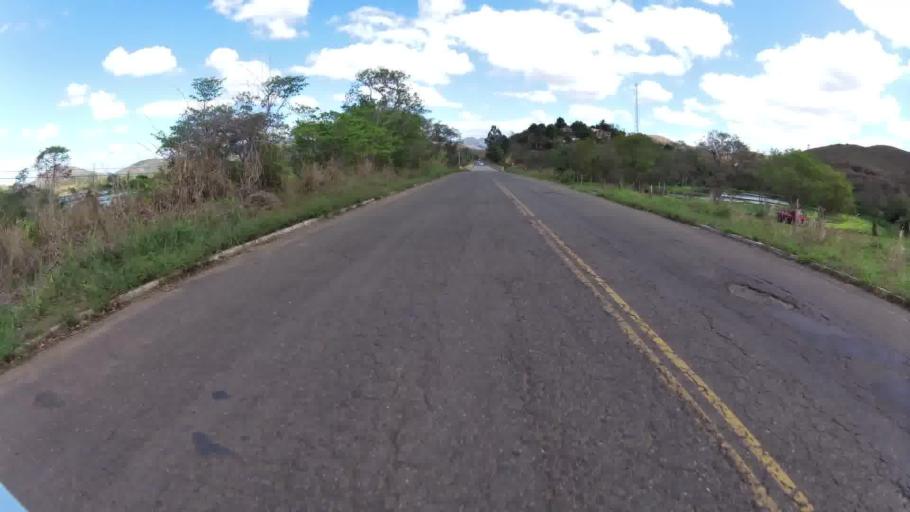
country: BR
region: Rio de Janeiro
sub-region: Itaperuna
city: Itaperuna
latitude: -21.2722
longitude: -41.7827
